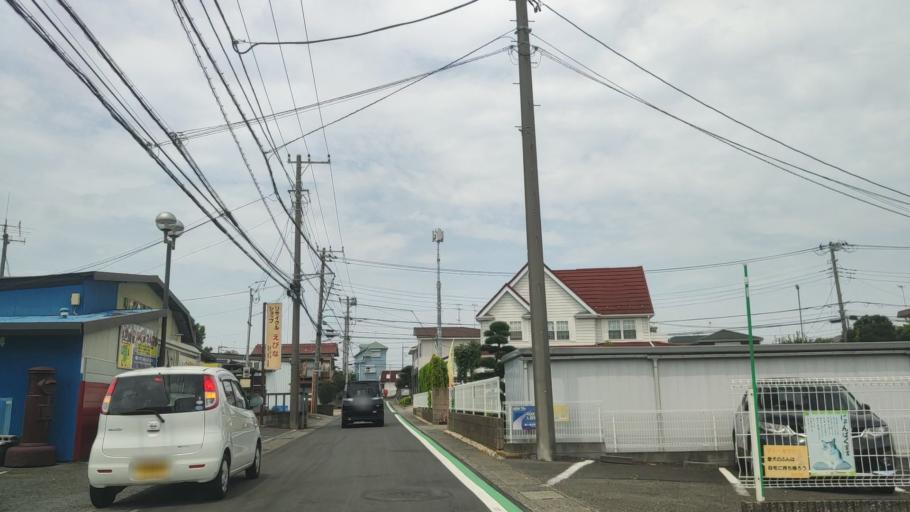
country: JP
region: Kanagawa
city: Atsugi
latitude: 35.4325
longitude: 139.3952
